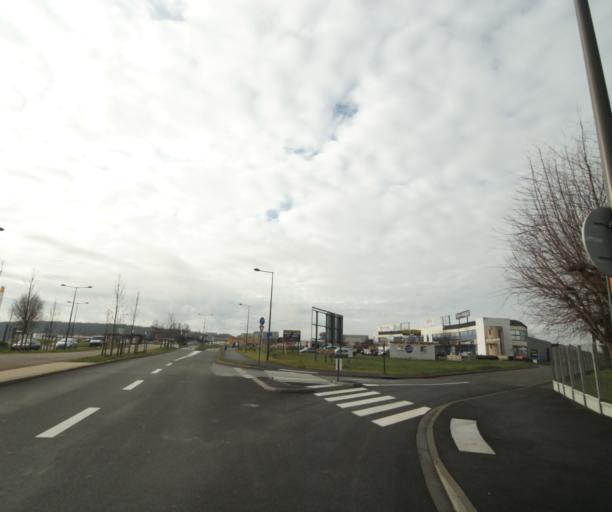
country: FR
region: Pays de la Loire
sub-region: Departement de la Sarthe
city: Allonnes
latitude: 47.9794
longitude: 0.1738
